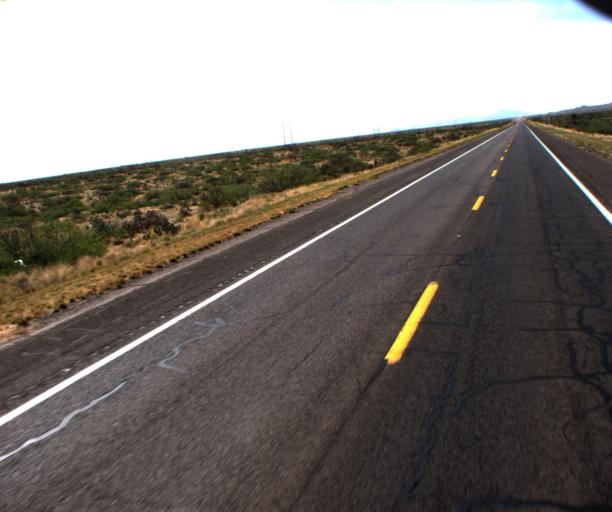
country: US
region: Arizona
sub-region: Graham County
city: Swift Trail Junction
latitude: 32.6087
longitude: -109.6871
